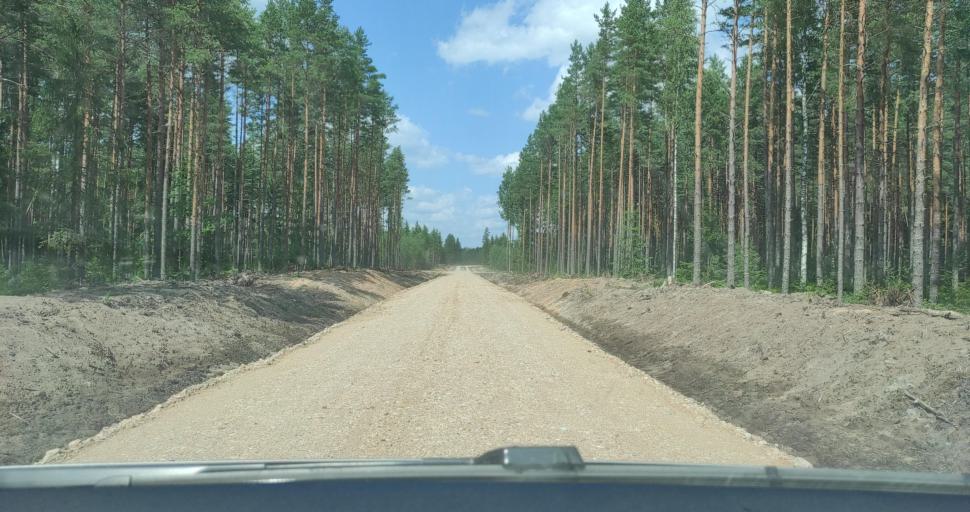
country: LV
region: Kuldigas Rajons
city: Kuldiga
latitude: 57.0561
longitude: 22.1900
